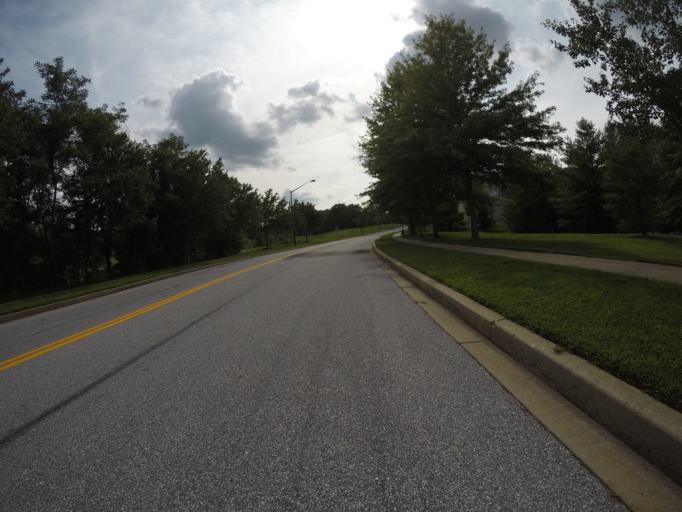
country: US
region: Maryland
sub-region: Howard County
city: Columbia
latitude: 39.3138
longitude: -76.8804
